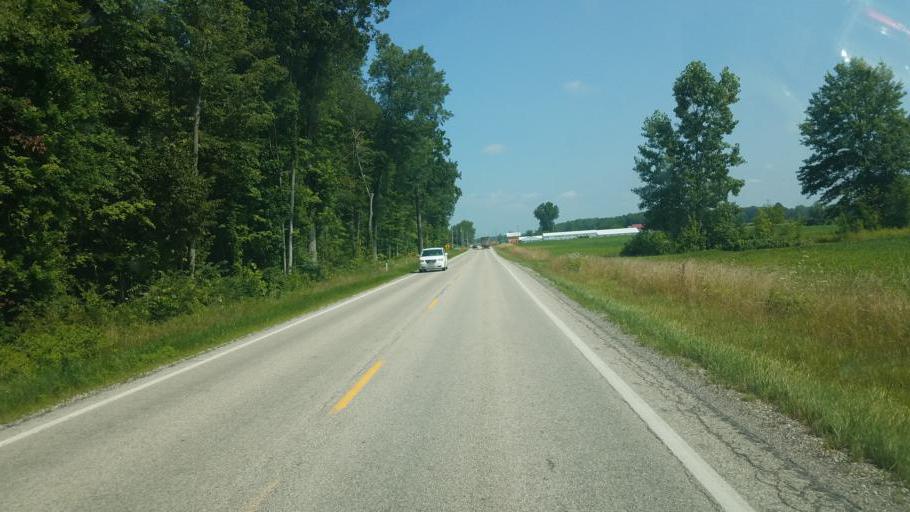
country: US
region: Ohio
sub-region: Crawford County
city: Galion
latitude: 40.8097
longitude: -82.8561
